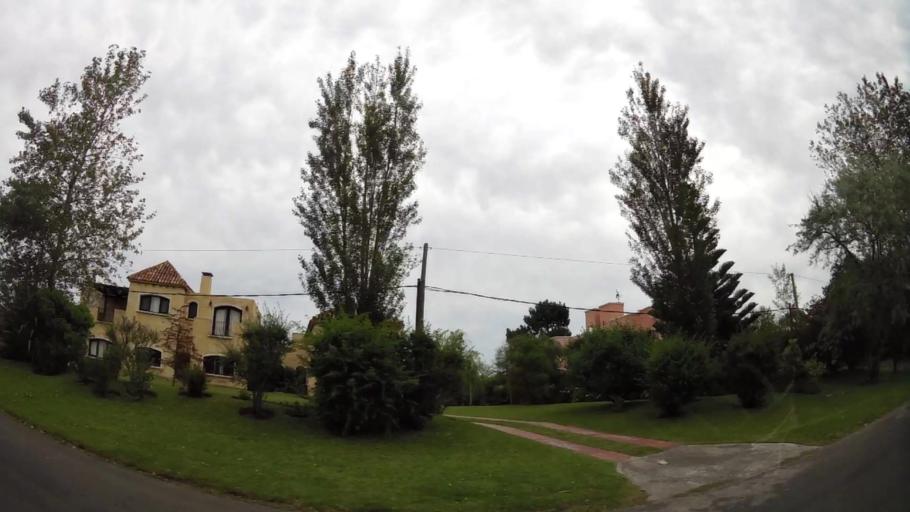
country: UY
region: Maldonado
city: Maldonado
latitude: -34.9074
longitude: -54.9958
